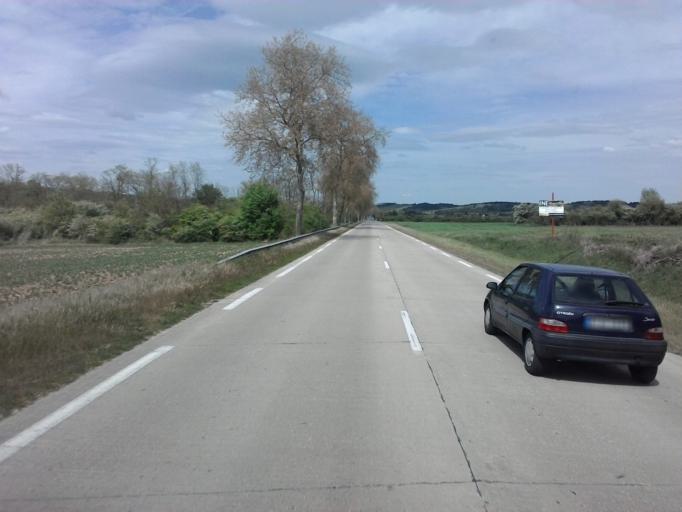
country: FR
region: Bourgogne
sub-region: Departement de l'Yonne
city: Augy
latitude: 47.7539
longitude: 3.6066
